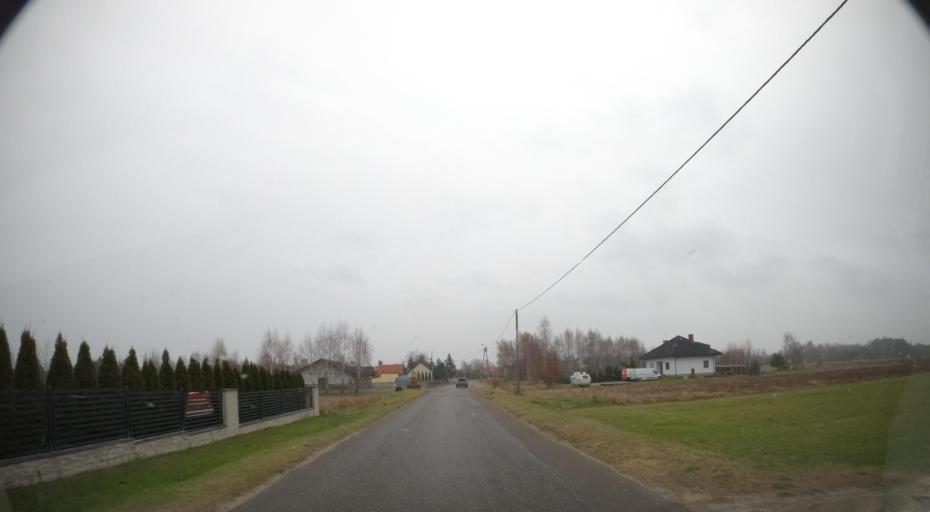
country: PL
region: Masovian Voivodeship
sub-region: Powiat radomski
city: Jedlnia-Letnisko
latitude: 51.4155
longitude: 21.2632
